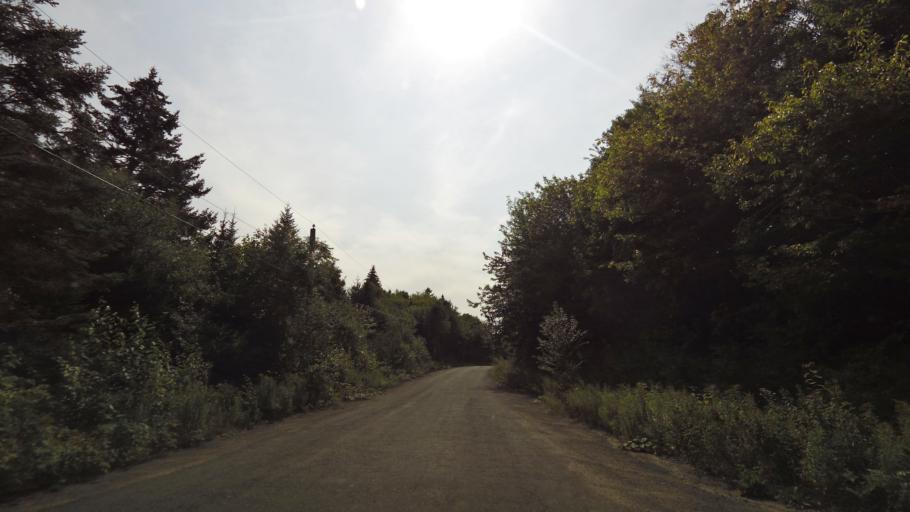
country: CA
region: New Brunswick
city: Hampton
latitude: 45.5726
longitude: -65.8317
